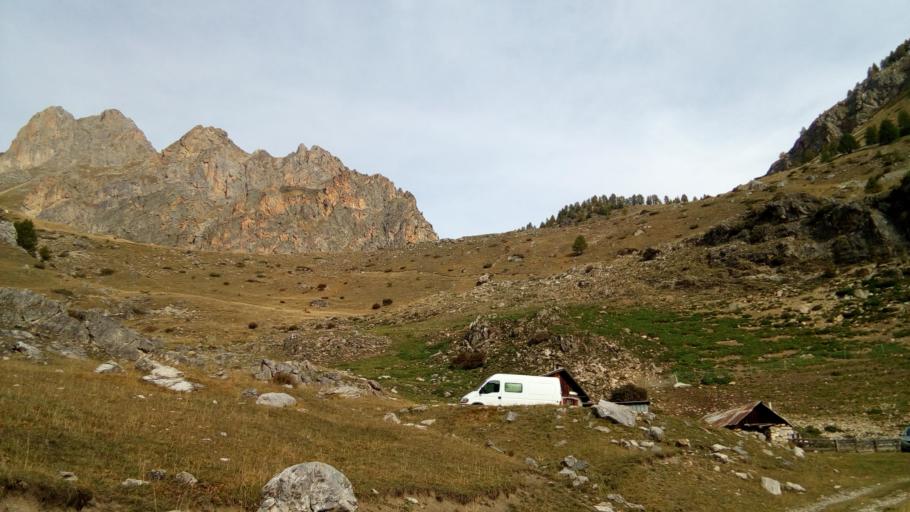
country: FR
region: Provence-Alpes-Cote d'Azur
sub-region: Departement des Hautes-Alpes
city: Guillestre
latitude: 44.7089
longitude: 6.5415
